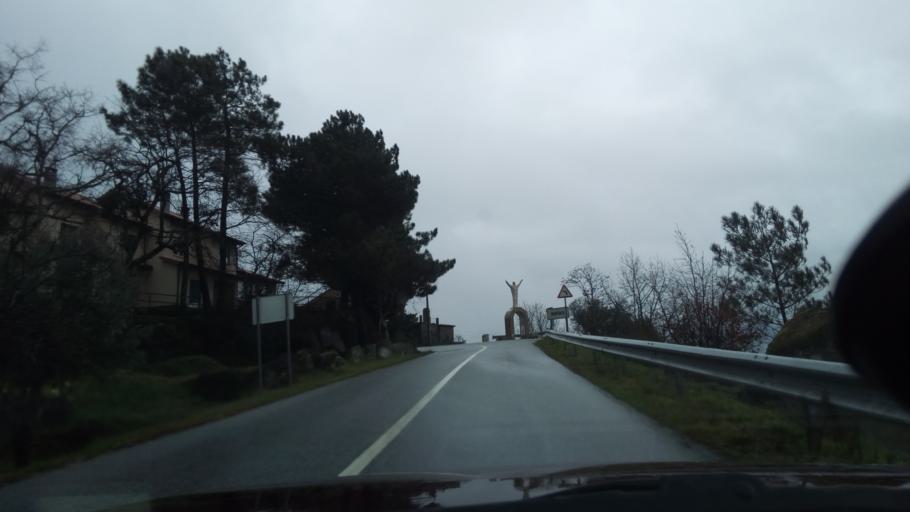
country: PT
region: Guarda
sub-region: Fornos de Algodres
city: Fornos de Algodres
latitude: 40.6301
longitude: -7.5355
